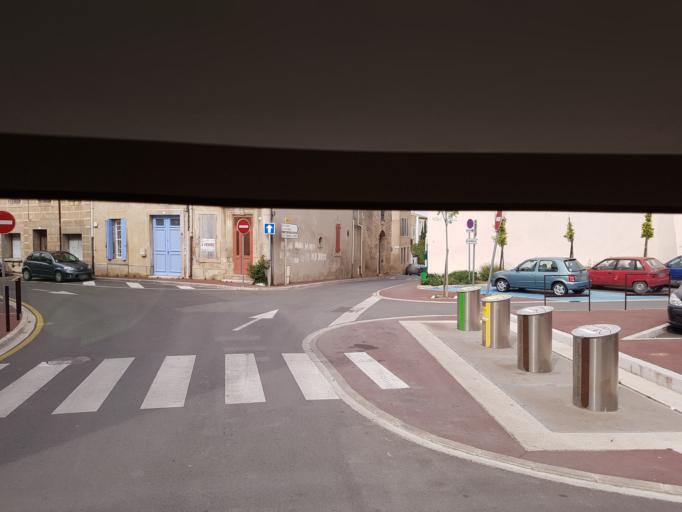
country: FR
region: Languedoc-Roussillon
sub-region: Departement de l'Aude
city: Fleury
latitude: 43.2296
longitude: 3.1360
